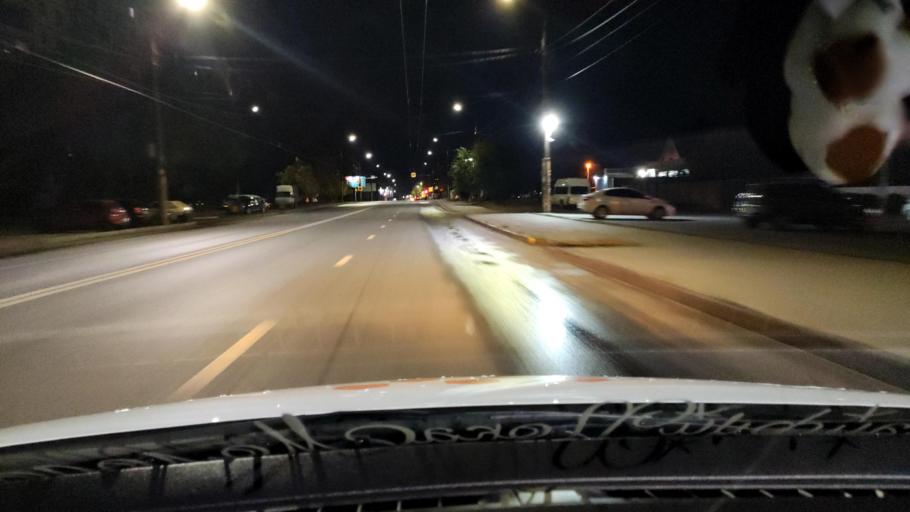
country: RU
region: Voronezj
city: Podgornoye
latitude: 51.7014
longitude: 39.1521
